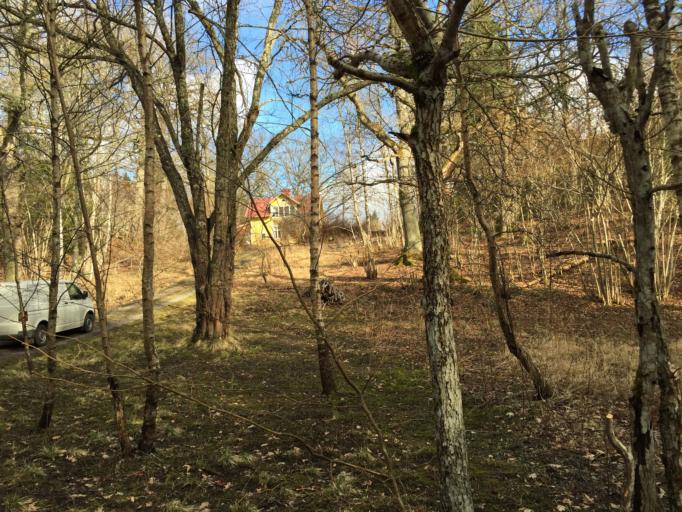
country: SE
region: Stockholm
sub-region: Salems Kommun
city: Ronninge
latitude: 59.1852
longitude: 17.7137
